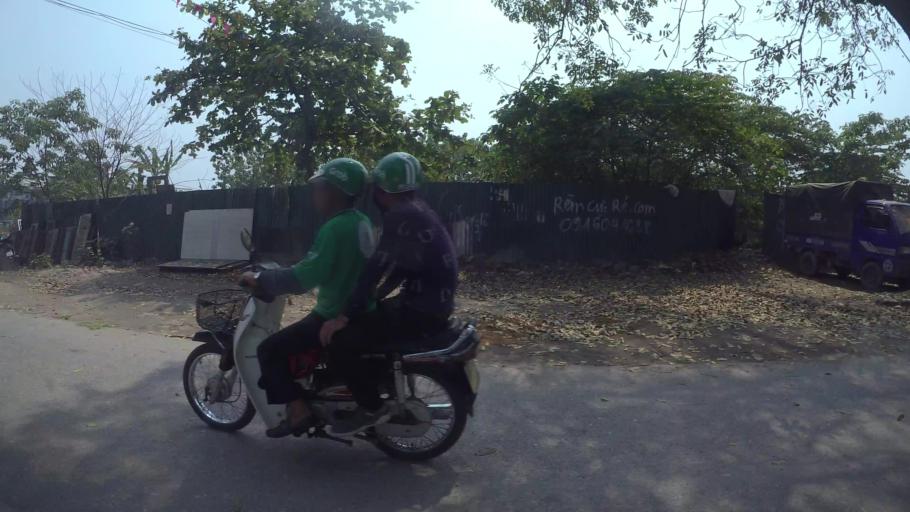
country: VN
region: Ha Noi
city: Ha Dong
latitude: 20.9905
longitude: 105.7638
